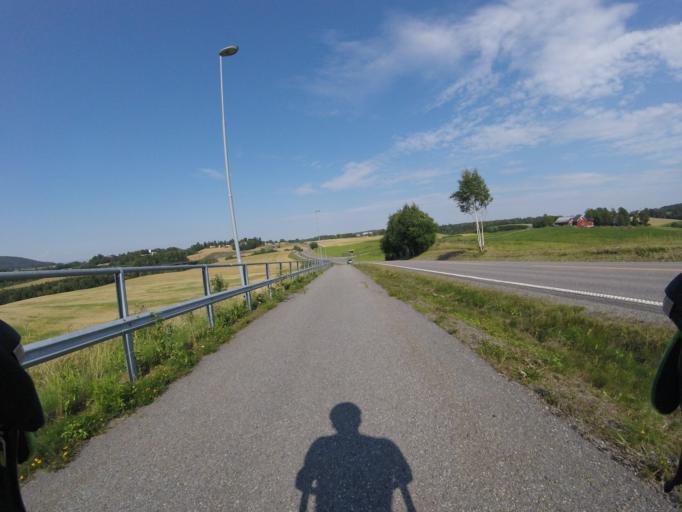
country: NO
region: Akershus
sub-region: Sorum
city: Frogner
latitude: 60.0085
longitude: 11.1076
